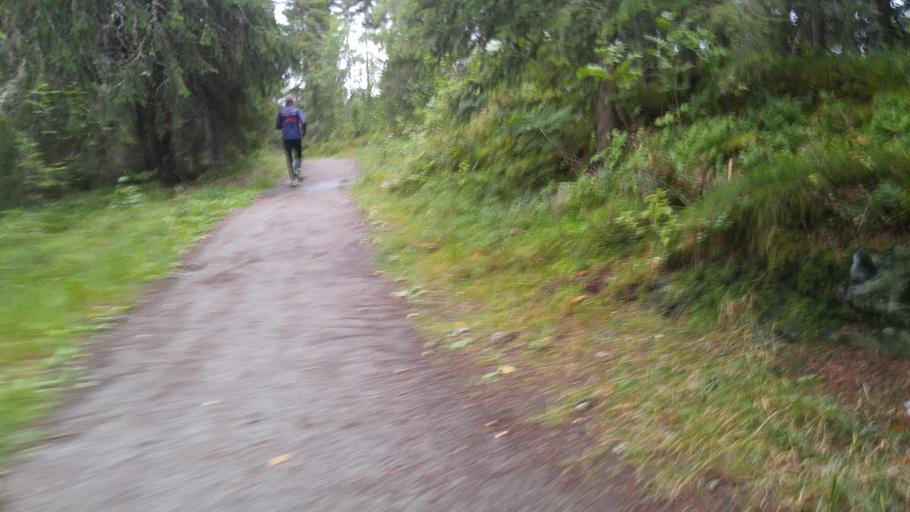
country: NO
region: Sor-Trondelag
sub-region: Trondheim
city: Trondheim
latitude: 63.4071
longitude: 10.3264
